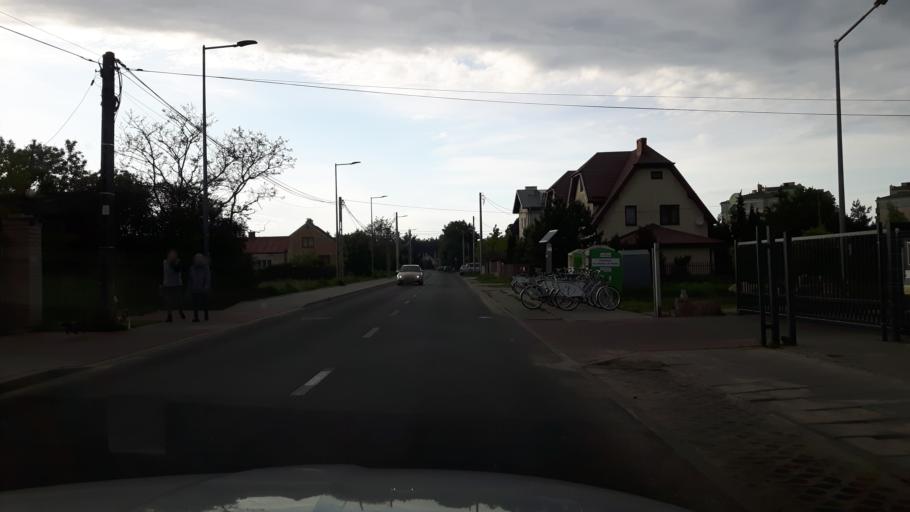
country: PL
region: Masovian Voivodeship
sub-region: Warszawa
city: Rembertow
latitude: 52.2710
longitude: 21.1500
